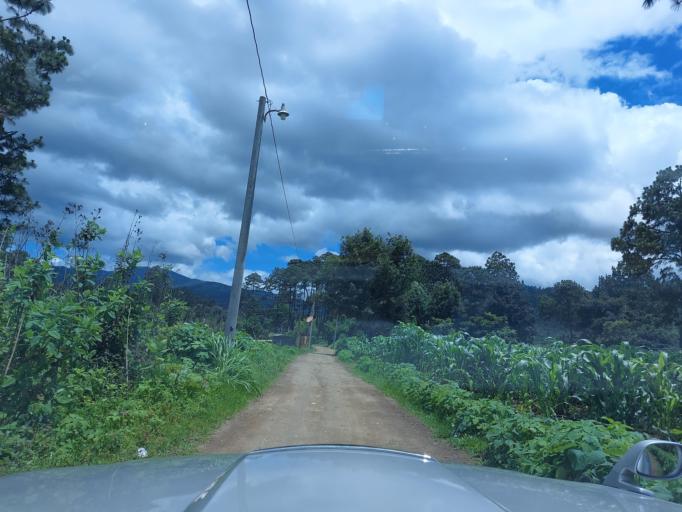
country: GT
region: Chimaltenango
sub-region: Municipio de Chimaltenango
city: Chimaltenango
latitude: 14.6437
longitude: -90.8262
